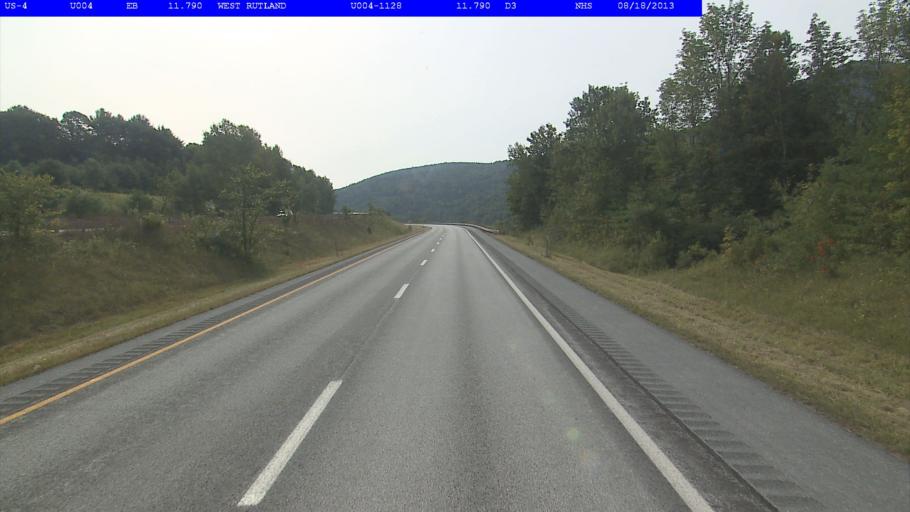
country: US
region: Vermont
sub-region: Rutland County
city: West Rutland
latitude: 43.6104
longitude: -73.0885
